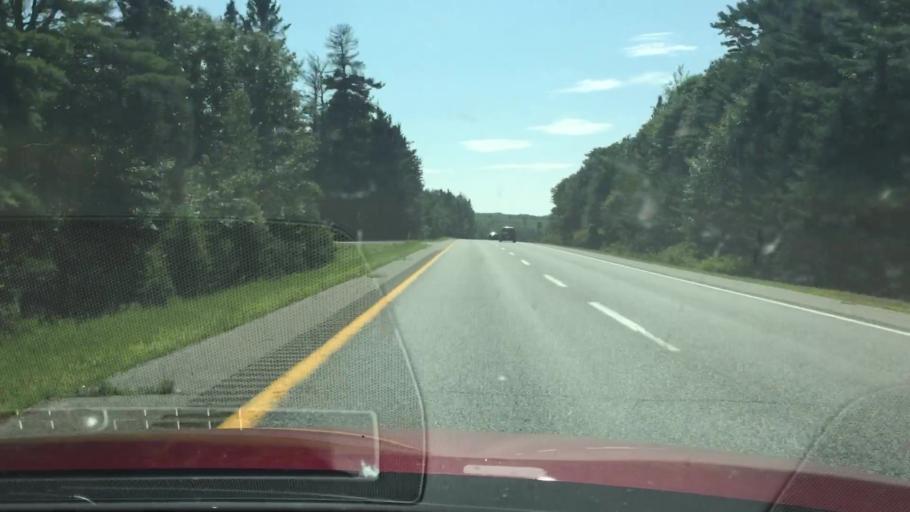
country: US
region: Maine
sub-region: Penobscot County
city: Veazie
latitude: 44.8685
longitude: -68.7066
